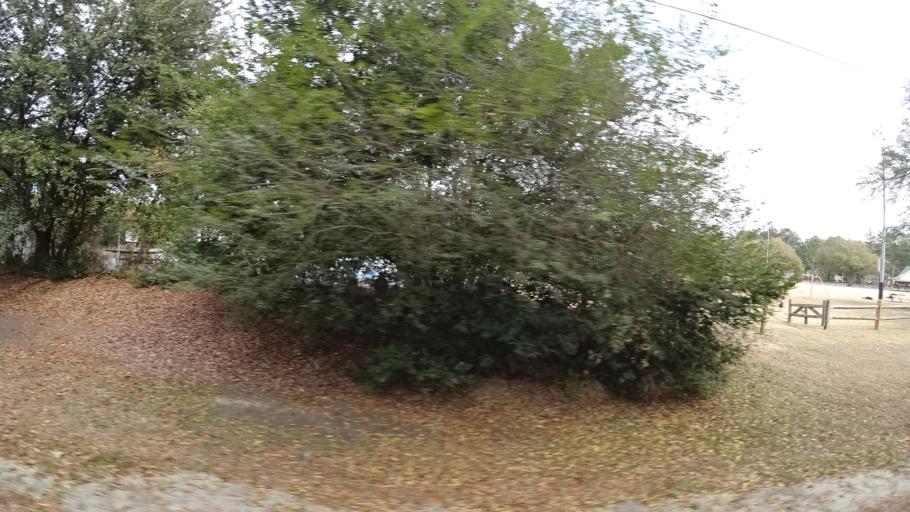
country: US
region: North Carolina
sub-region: Moore County
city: Pinehurst
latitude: 35.2040
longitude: -79.4655
